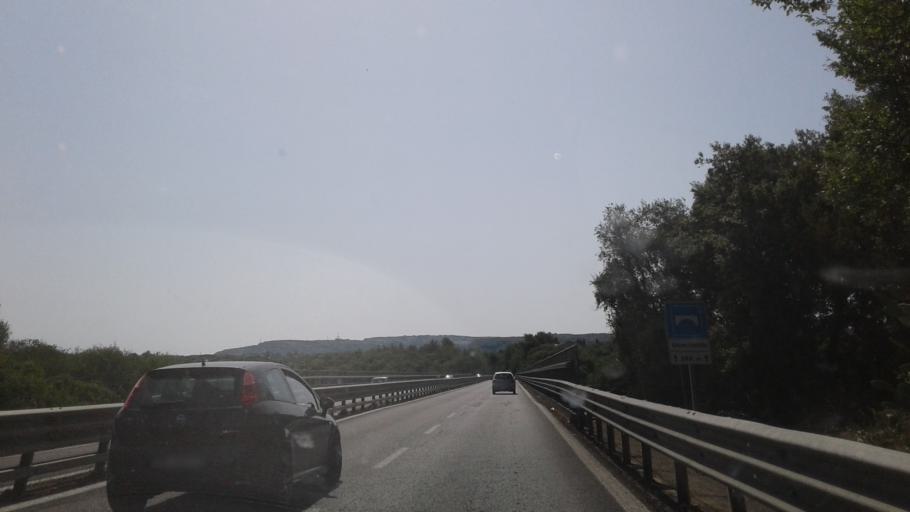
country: IT
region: Sardinia
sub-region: Provincia di Sassari
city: Tissi
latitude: 40.7021
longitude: 8.5552
